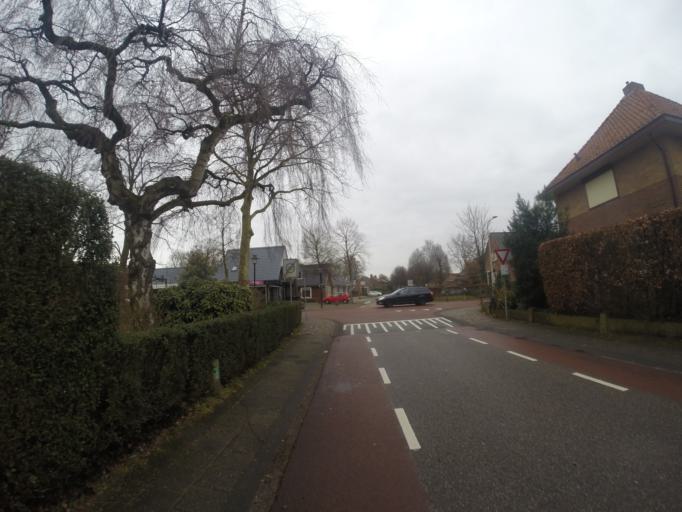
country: NL
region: Gelderland
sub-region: Gemeente Bronckhorst
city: Zelhem
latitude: 52.0056
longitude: 6.3486
